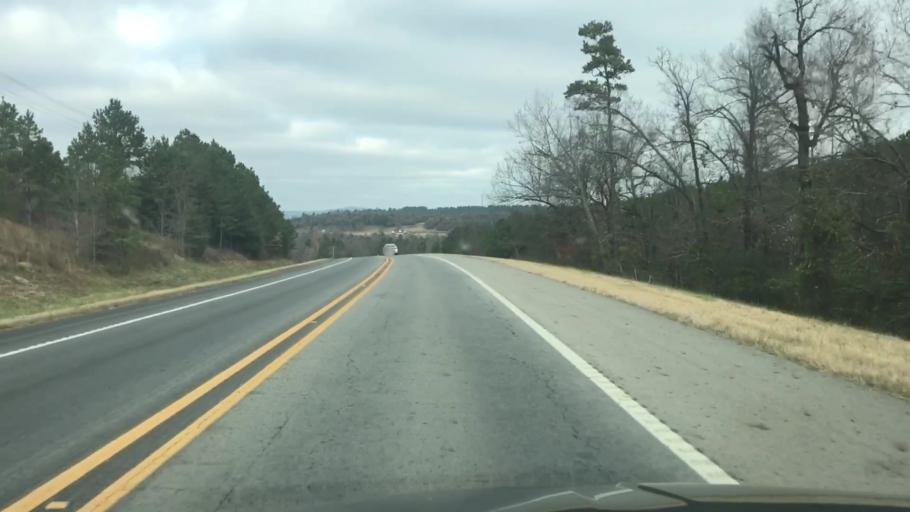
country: US
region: Arkansas
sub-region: Scott County
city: Waldron
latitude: 34.8426
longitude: -94.0544
